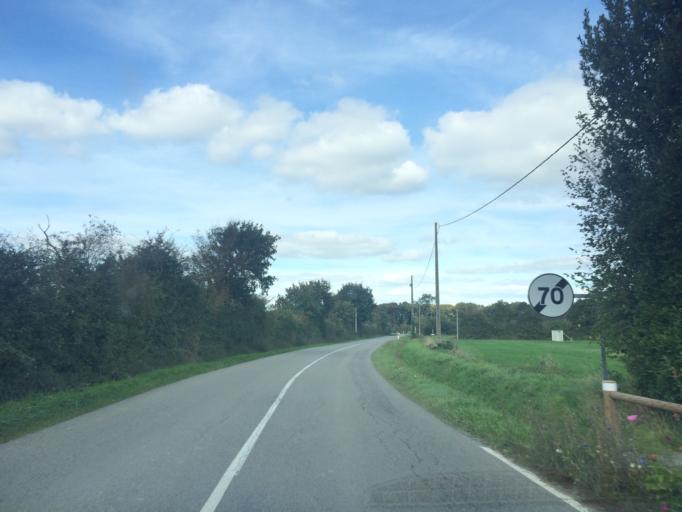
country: FR
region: Pays de la Loire
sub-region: Departement de la Loire-Atlantique
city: Chemere
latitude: 47.1306
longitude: -1.9105
